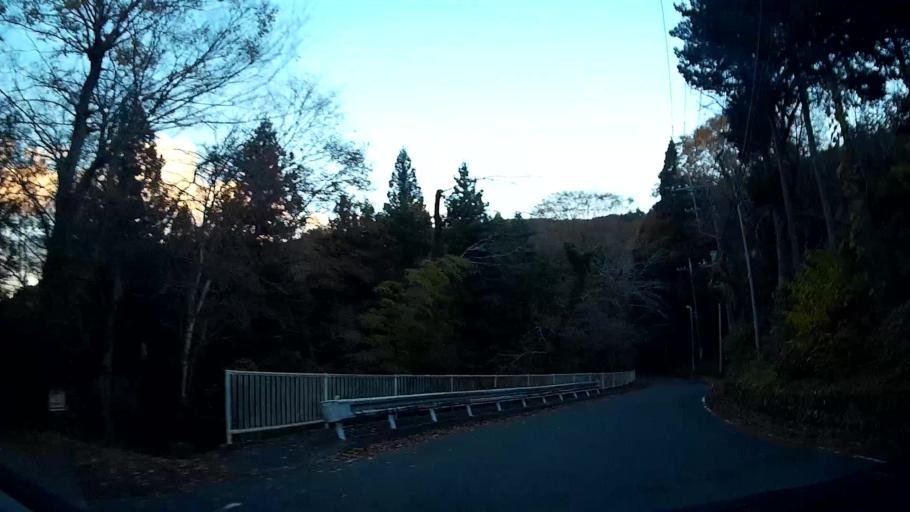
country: JP
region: Yamanashi
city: Uenohara
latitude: 35.5583
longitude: 139.1771
